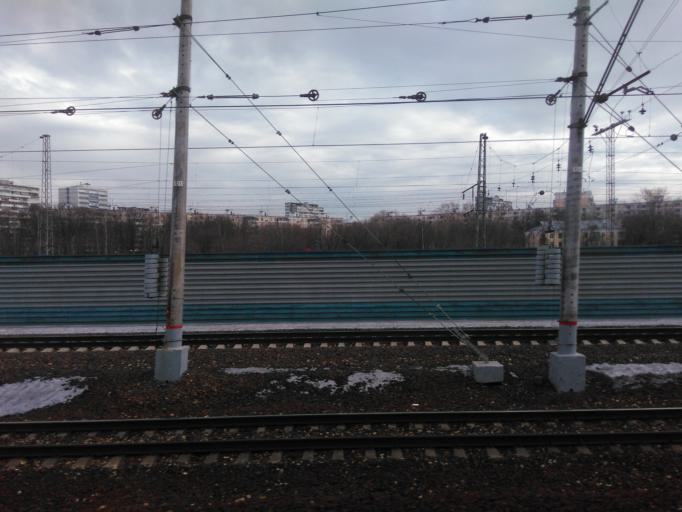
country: RU
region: Moscow
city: Vatutino
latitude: 55.8669
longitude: 37.6898
